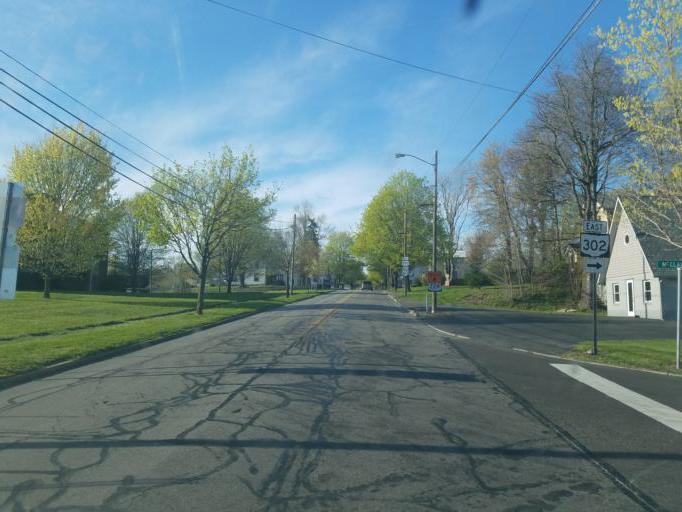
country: US
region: Ohio
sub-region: Ashland County
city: Ashland
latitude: 40.9616
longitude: -82.3646
